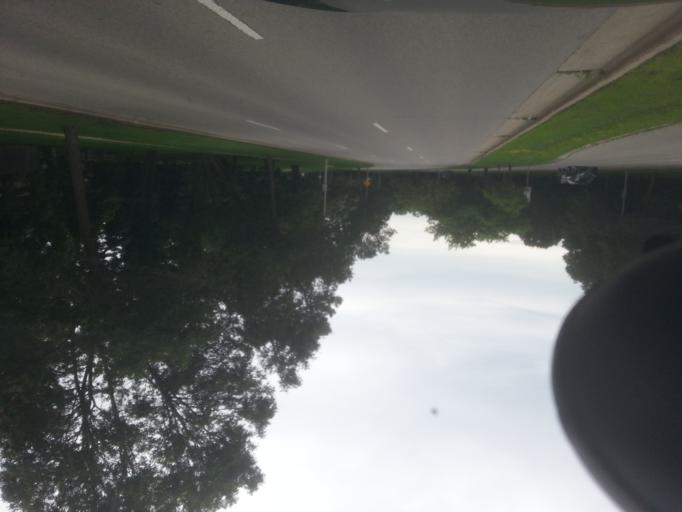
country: US
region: Wisconsin
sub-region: Dane County
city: Shorewood Hills
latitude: 43.0614
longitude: -89.4722
